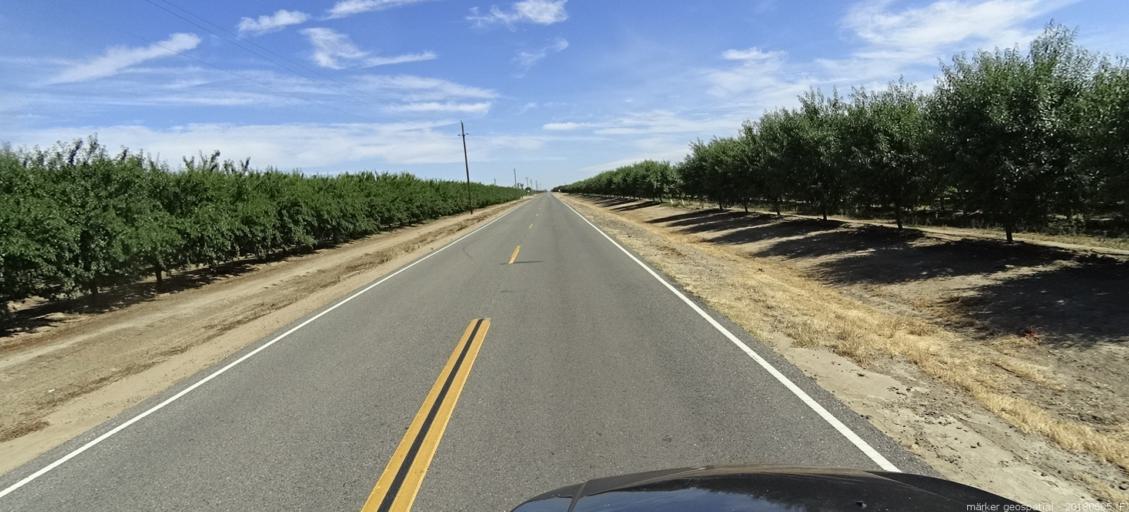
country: US
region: California
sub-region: Madera County
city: Chowchilla
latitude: 37.0554
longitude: -120.3830
